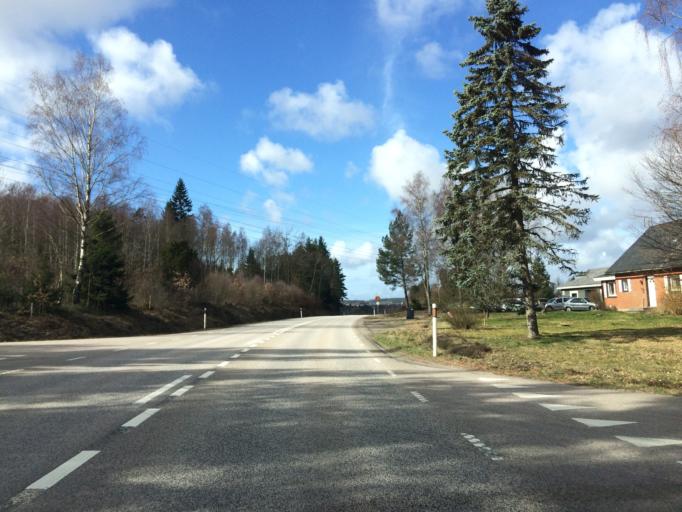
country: SE
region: Halland
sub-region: Laholms Kommun
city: Knared
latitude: 56.5002
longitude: 13.3652
